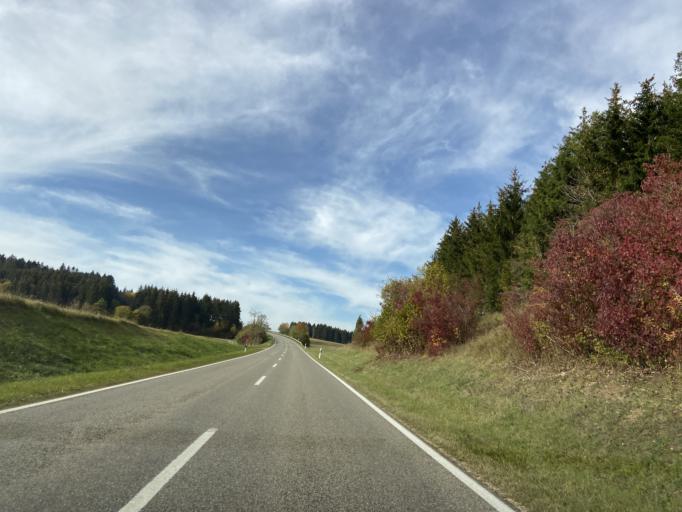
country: DE
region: Baden-Wuerttemberg
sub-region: Tuebingen Region
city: Messkirch
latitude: 48.0540
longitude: 9.0844
